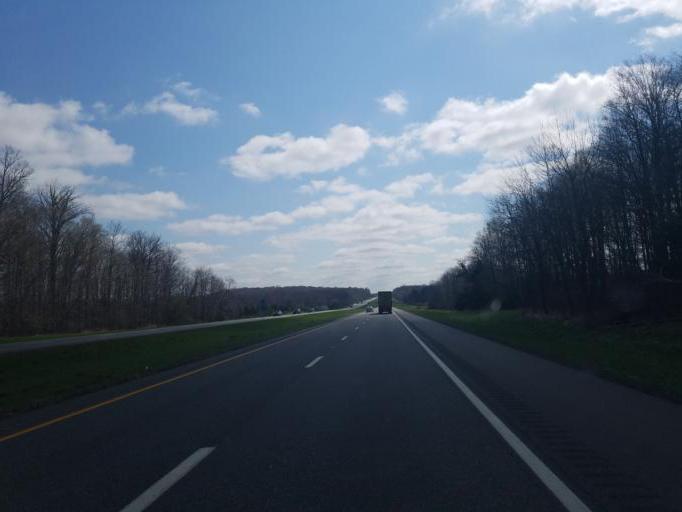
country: US
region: Ohio
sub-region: Geauga County
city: Bainbridge
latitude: 41.3846
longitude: -81.3167
